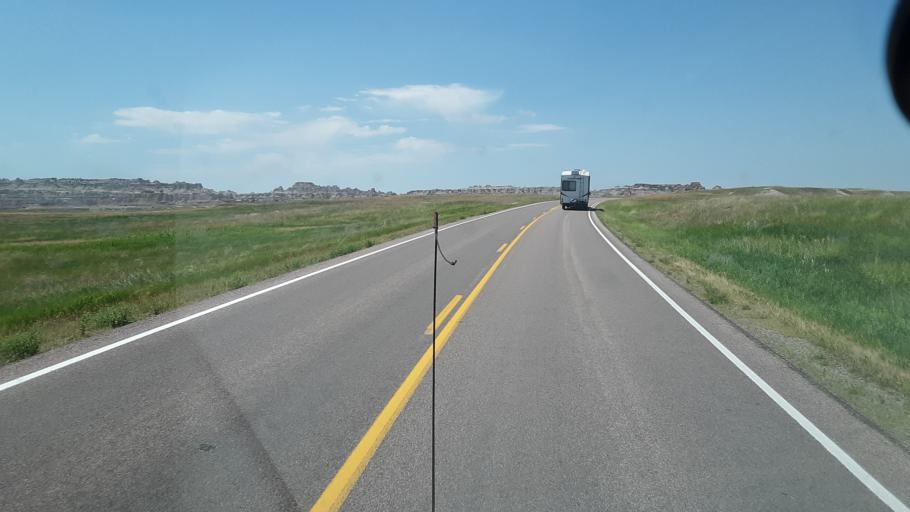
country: US
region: South Dakota
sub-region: Haakon County
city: Philip
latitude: 43.7724
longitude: -101.9161
